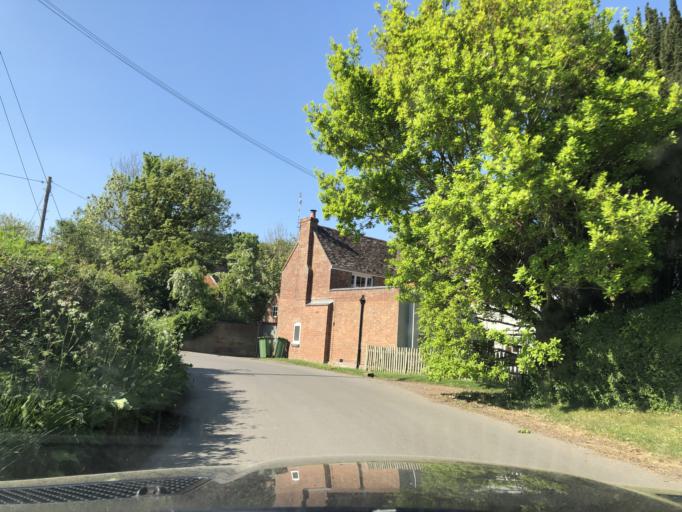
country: GB
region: England
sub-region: Warwickshire
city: Warwick
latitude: 52.2877
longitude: -1.6230
